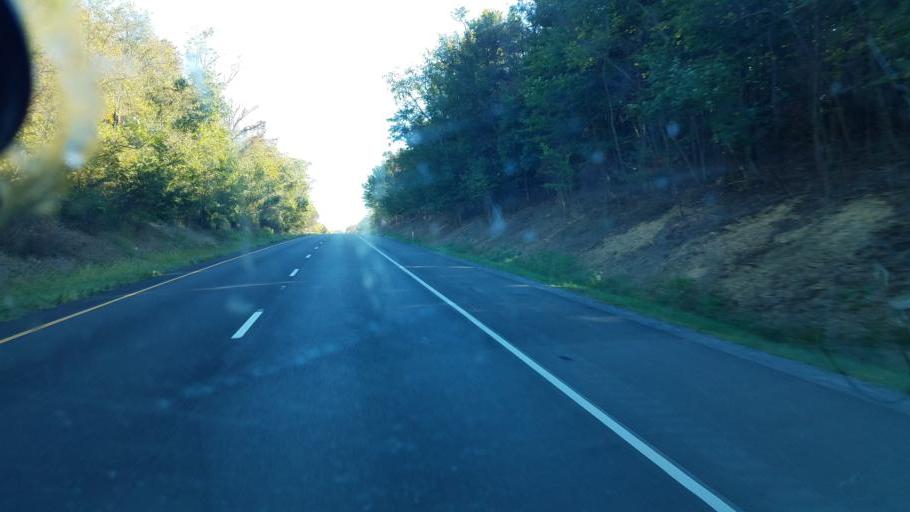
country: US
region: Maryland
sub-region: Washington County
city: Wilson-Conococheague
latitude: 39.6313
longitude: -77.9631
